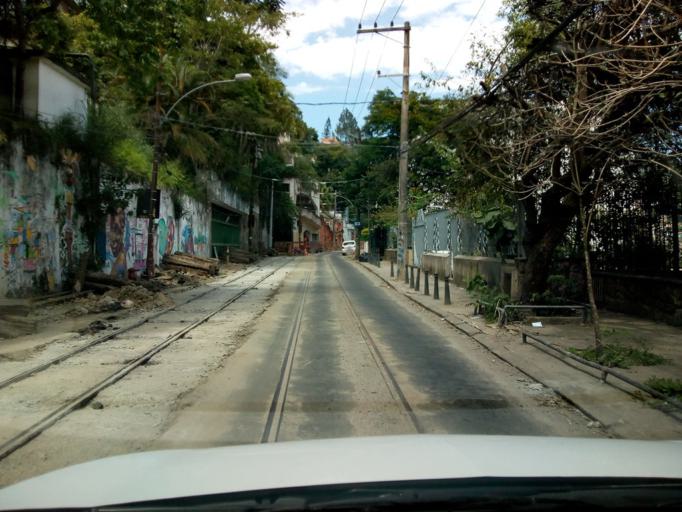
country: BR
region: Rio de Janeiro
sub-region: Rio De Janeiro
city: Rio de Janeiro
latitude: -22.9312
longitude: -43.1960
